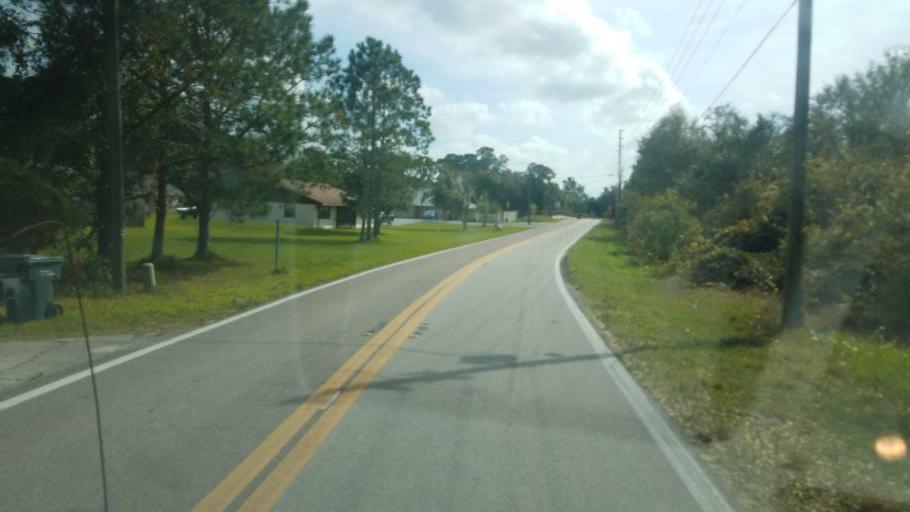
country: US
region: Florida
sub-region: Polk County
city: Lake Wales
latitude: 27.9635
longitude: -81.5400
